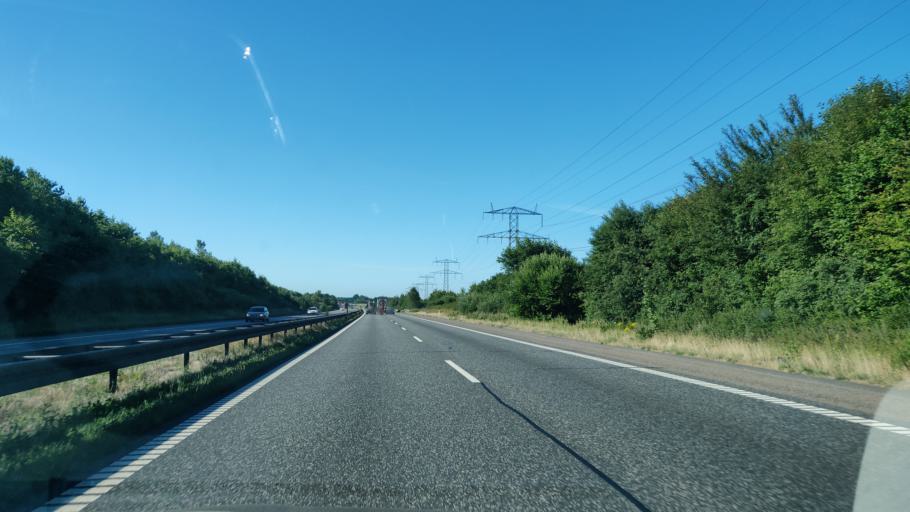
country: DK
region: Central Jutland
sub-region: Arhus Kommune
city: Trige
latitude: 56.2517
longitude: 10.1245
